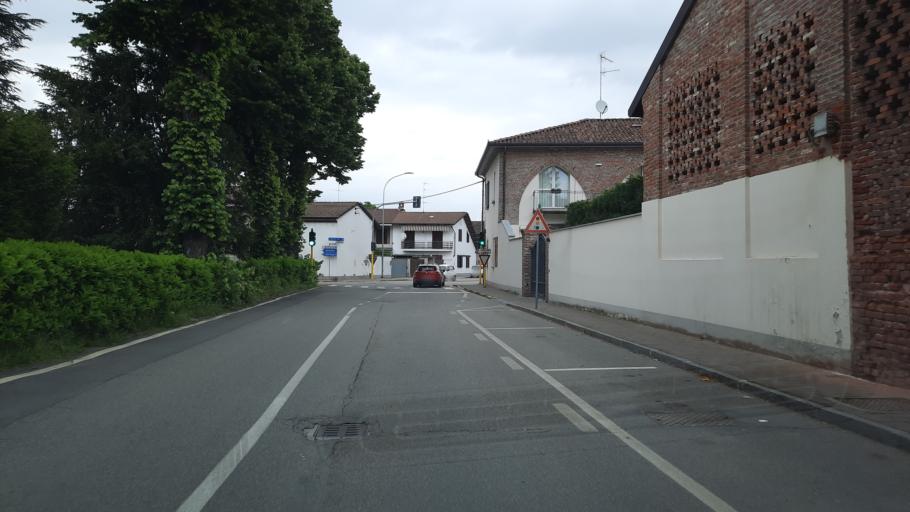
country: IT
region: Lombardy
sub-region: Provincia di Pavia
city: Robbio
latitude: 45.2901
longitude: 8.5918
